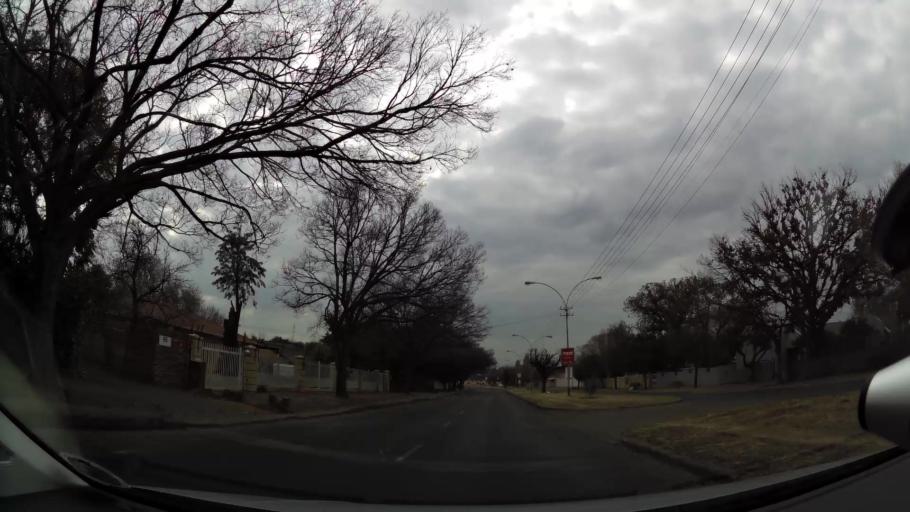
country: ZA
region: Orange Free State
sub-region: Mangaung Metropolitan Municipality
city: Bloemfontein
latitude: -29.0916
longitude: 26.2150
